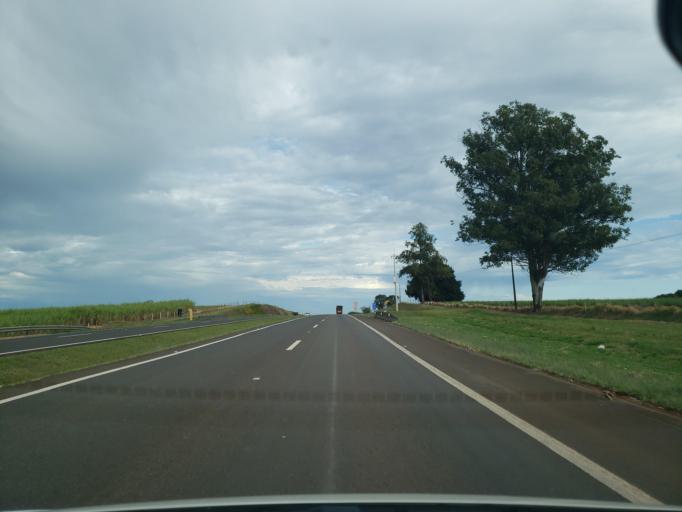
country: BR
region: Sao Paulo
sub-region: Jau
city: Jau
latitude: -22.2664
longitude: -48.4478
